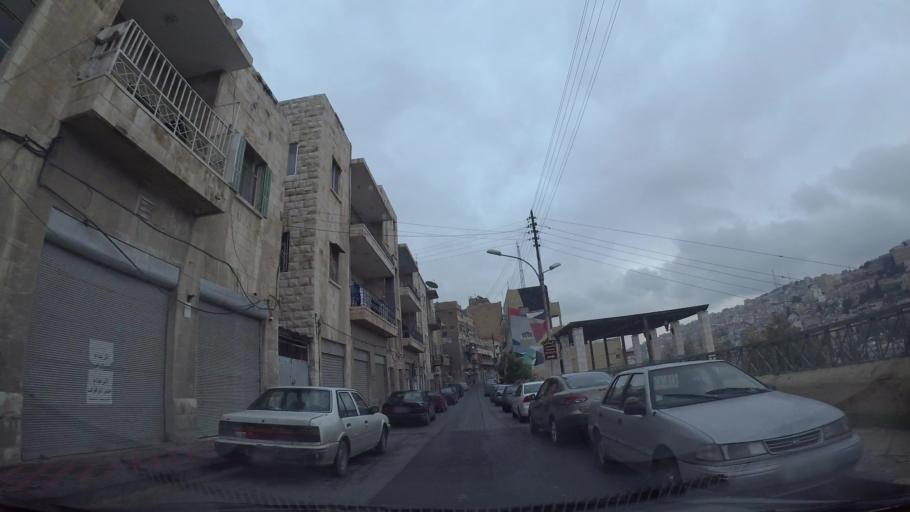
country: JO
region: Amman
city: Amman
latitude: 31.9536
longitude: 35.9384
